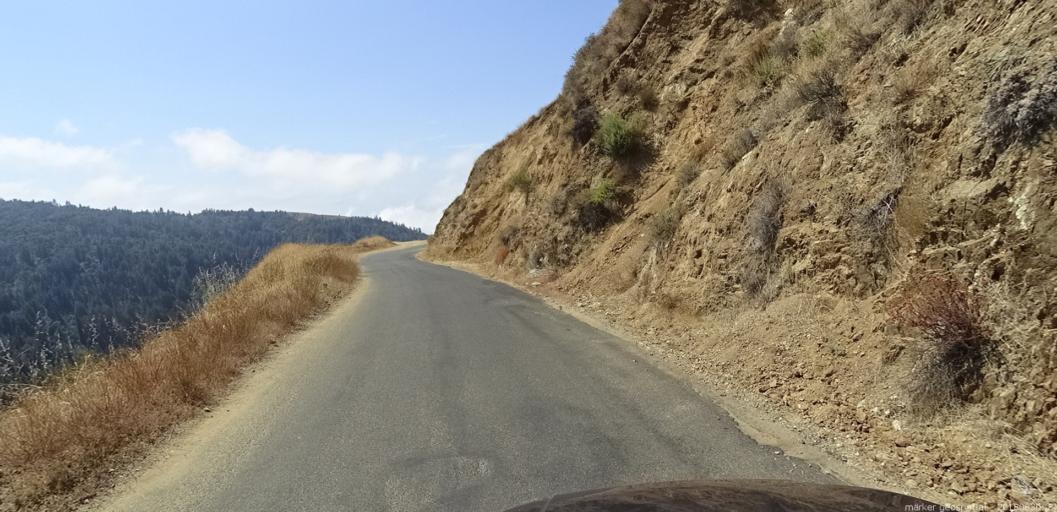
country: US
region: California
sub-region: Monterey County
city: Greenfield
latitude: 35.9974
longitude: -121.4591
